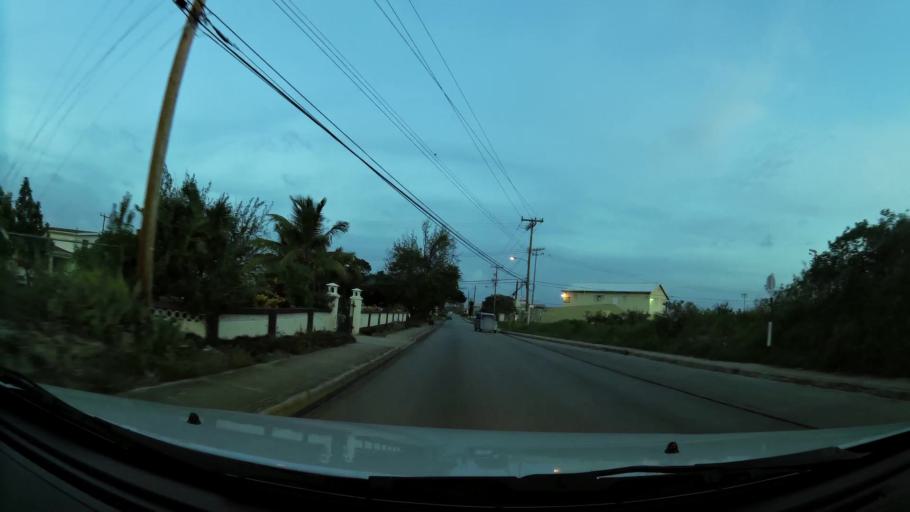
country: BB
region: Saint Philip
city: Crane
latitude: 13.1043
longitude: -59.4564
